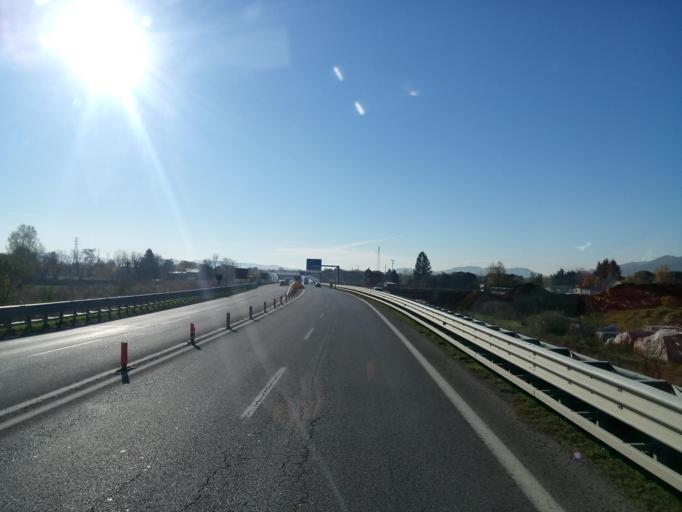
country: IT
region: Veneto
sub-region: Provincia di Vicenza
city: Tezze
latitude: 45.5167
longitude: 11.3871
